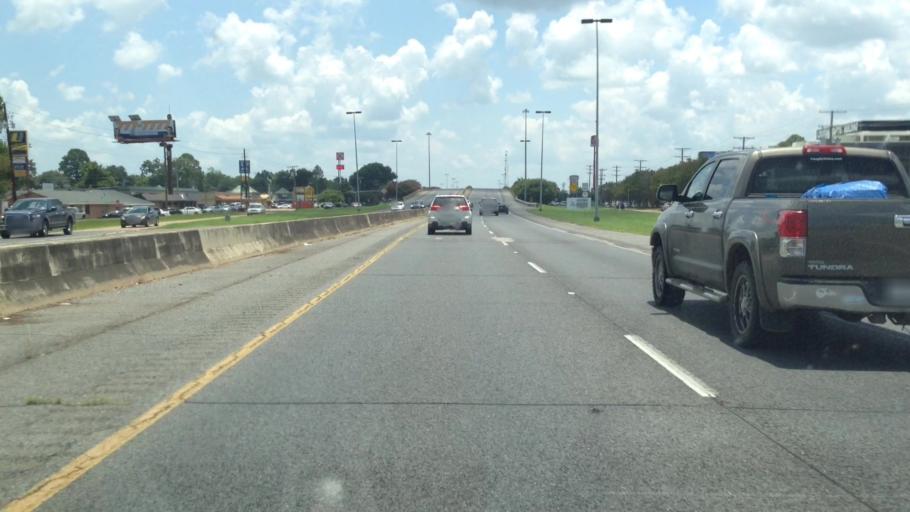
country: US
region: Louisiana
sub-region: Rapides Parish
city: Alexandria
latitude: 31.2894
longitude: -92.4762
